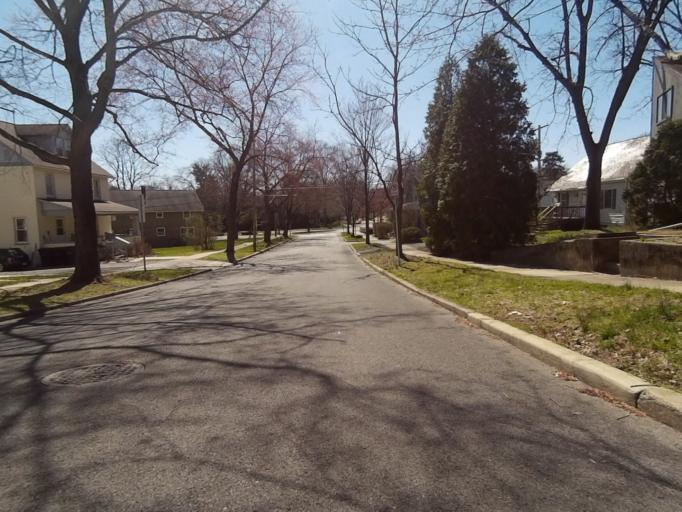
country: US
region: Pennsylvania
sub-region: Centre County
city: State College
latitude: 40.7902
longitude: -77.8521
